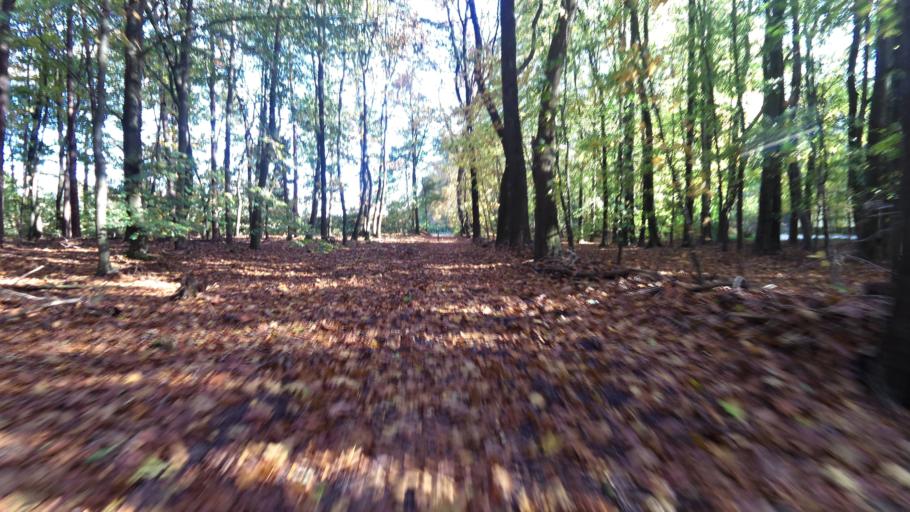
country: NL
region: Gelderland
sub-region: Gemeente Heerde
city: Heerde
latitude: 52.3954
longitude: 6.0029
